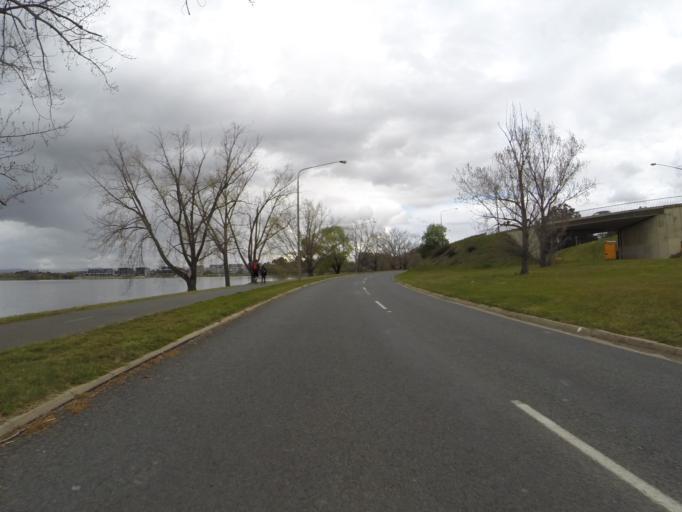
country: AU
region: Australian Capital Territory
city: Forrest
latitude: -35.3037
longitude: 149.1404
